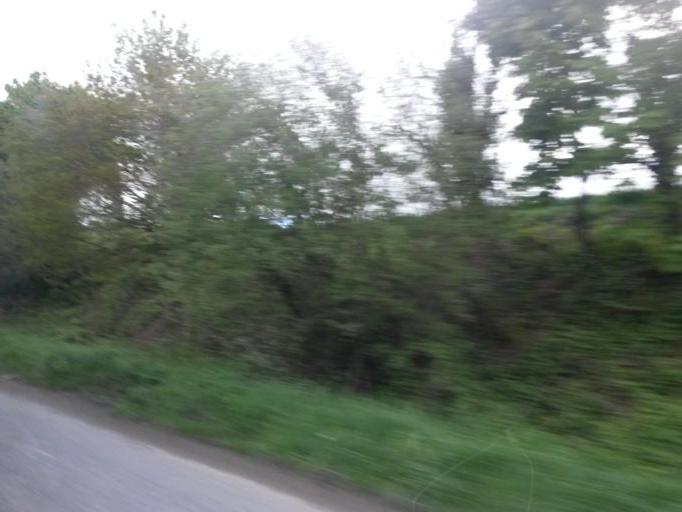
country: IE
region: Leinster
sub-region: Loch Garman
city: Enniscorthy
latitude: 52.4851
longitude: -6.5651
